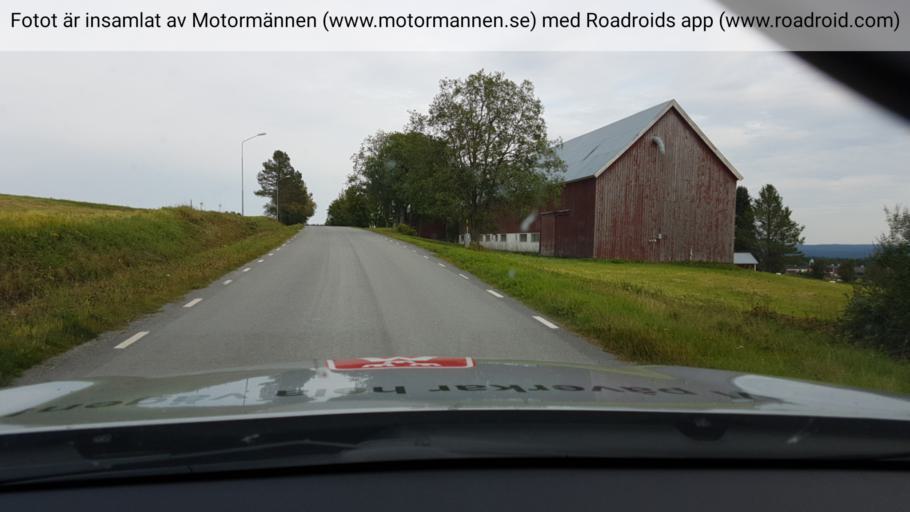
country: SE
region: Jaemtland
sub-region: OEstersunds Kommun
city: Lit
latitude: 63.6145
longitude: 14.9894
